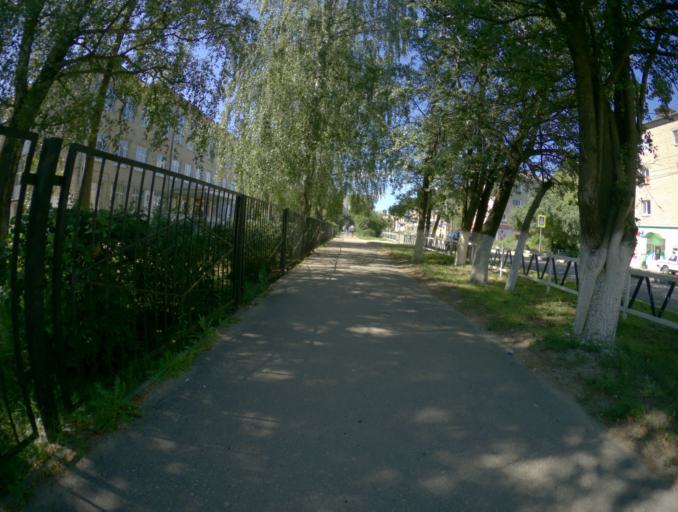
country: RU
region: Nizjnij Novgorod
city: Bor
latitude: 56.3561
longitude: 44.0686
